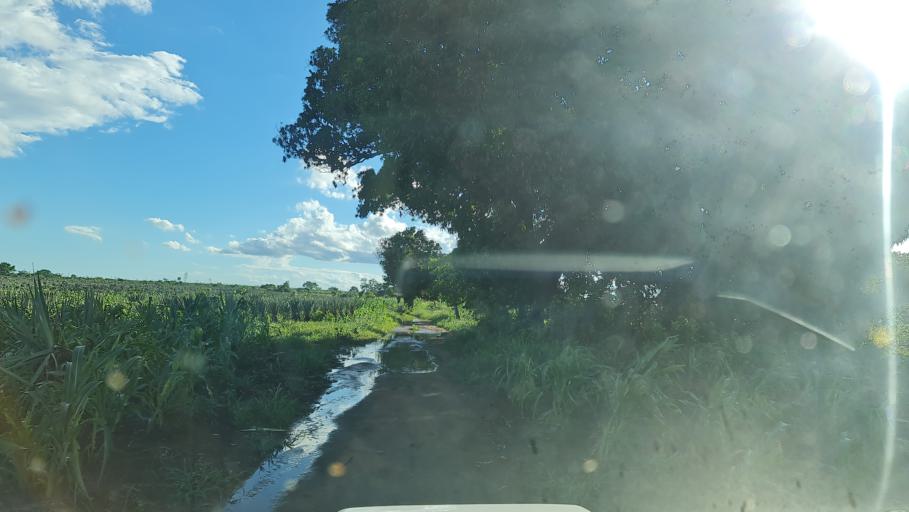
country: MZ
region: Nampula
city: Ilha de Mocambique
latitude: -14.9374
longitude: 40.2026
